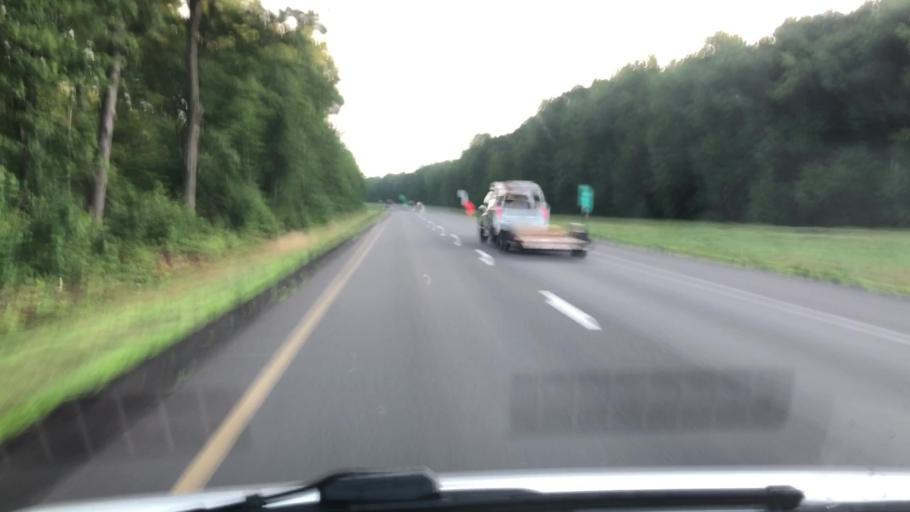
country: US
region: Massachusetts
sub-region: Franklin County
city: South Deerfield
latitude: 42.4855
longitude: -72.6160
